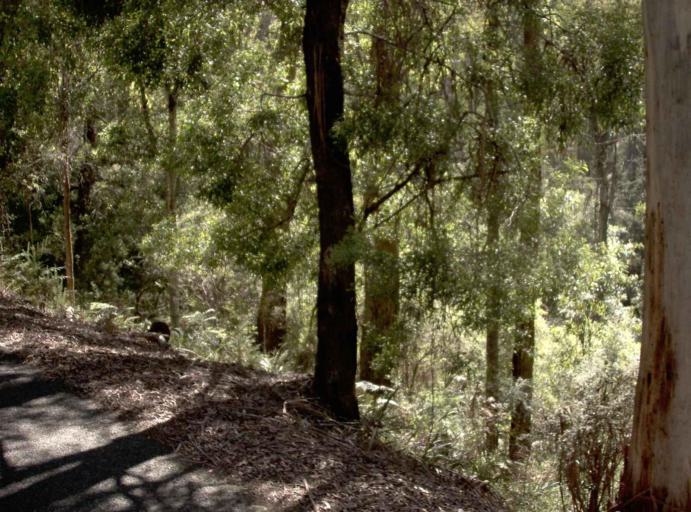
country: AU
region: New South Wales
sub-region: Bombala
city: Bombala
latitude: -37.3766
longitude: 148.6812
